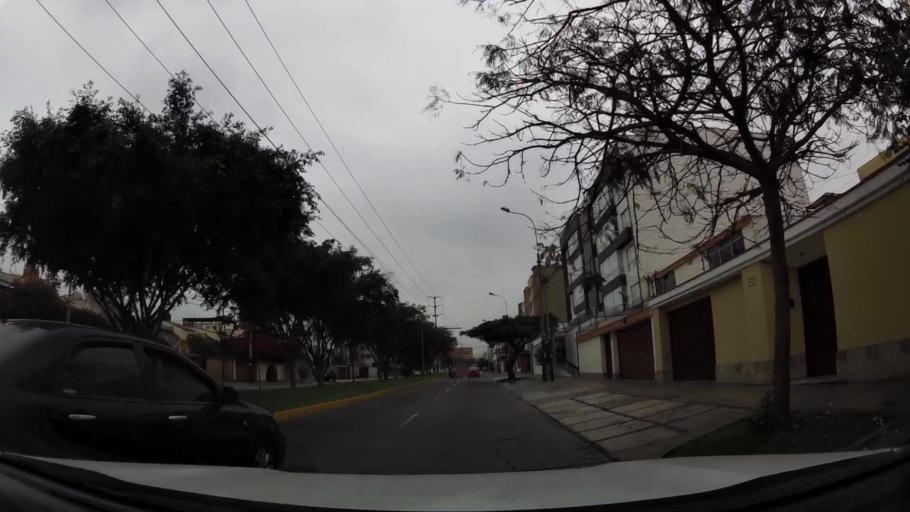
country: PE
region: Lima
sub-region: Lima
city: Surco
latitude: -12.1314
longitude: -77.0093
